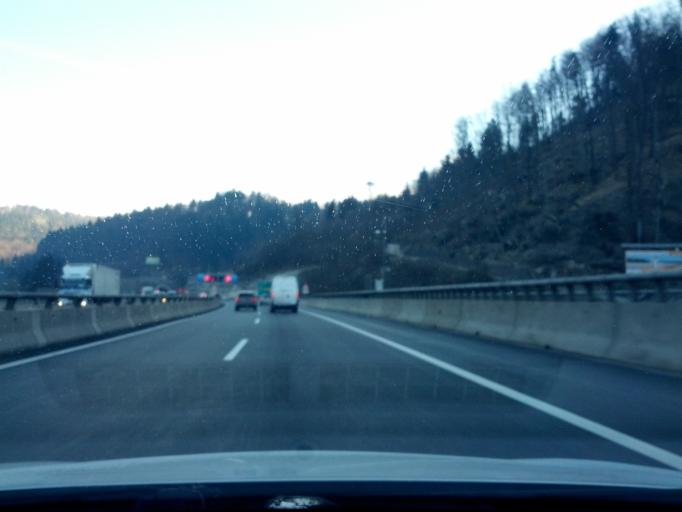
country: SI
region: Zagorje ob Savi
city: Izlake
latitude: 46.1817
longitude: 14.8549
